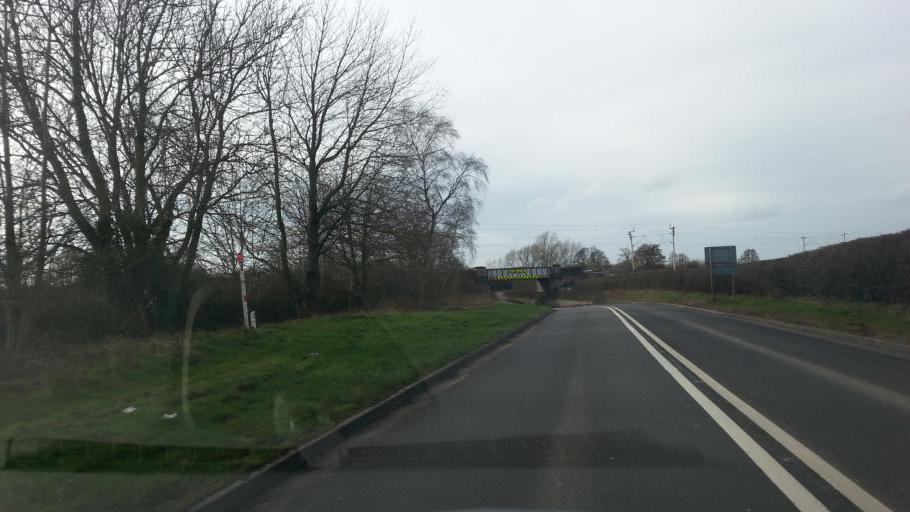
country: GB
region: England
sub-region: Staffordshire
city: Colwich
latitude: 52.8166
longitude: -2.0029
